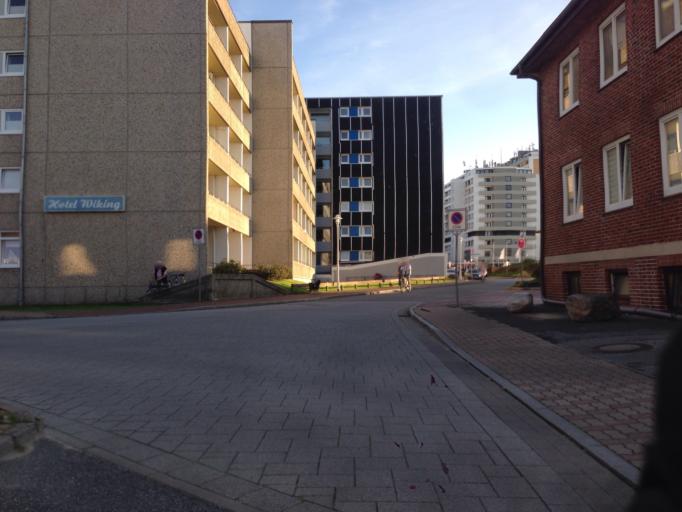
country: DE
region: Schleswig-Holstein
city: Westerland
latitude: 54.9107
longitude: 8.3019
